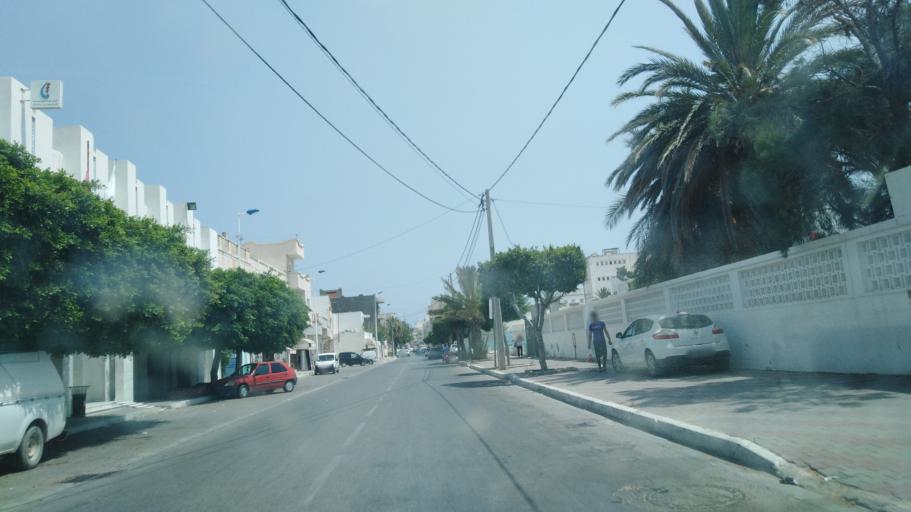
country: TN
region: Al Mahdiyah
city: Mahdia
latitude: 35.5110
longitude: 11.0491
